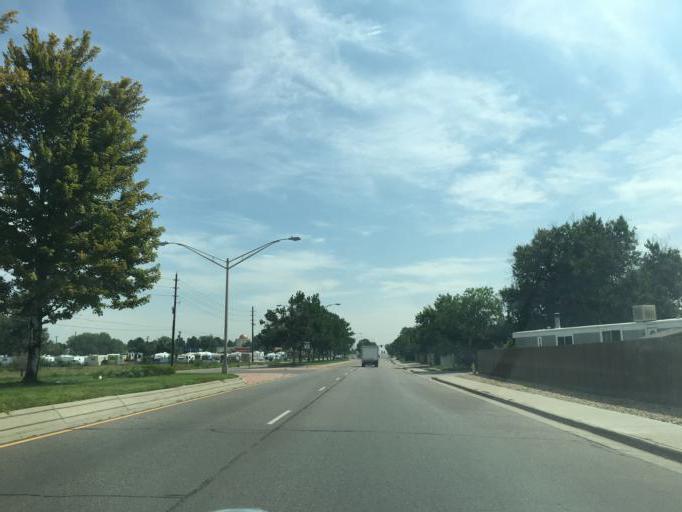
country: US
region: Colorado
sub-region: Adams County
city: Aurora
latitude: 39.7401
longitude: -104.8039
